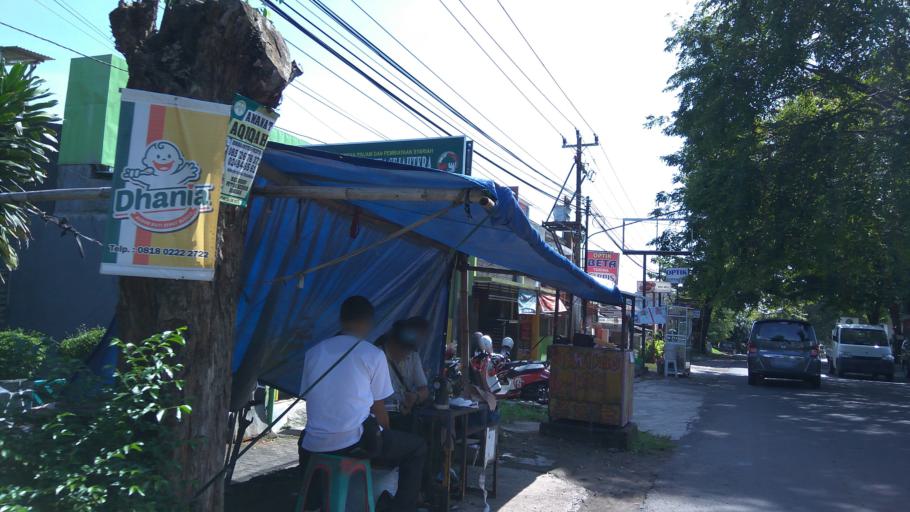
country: ID
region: Central Java
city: Ungaran
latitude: -7.0700
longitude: 110.4224
